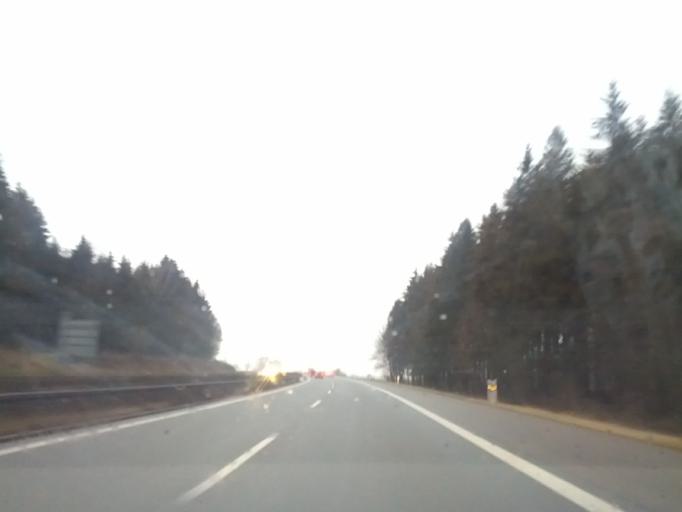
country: DE
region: Bavaria
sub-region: Swabia
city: Bohen
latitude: 47.8600
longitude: 10.2773
